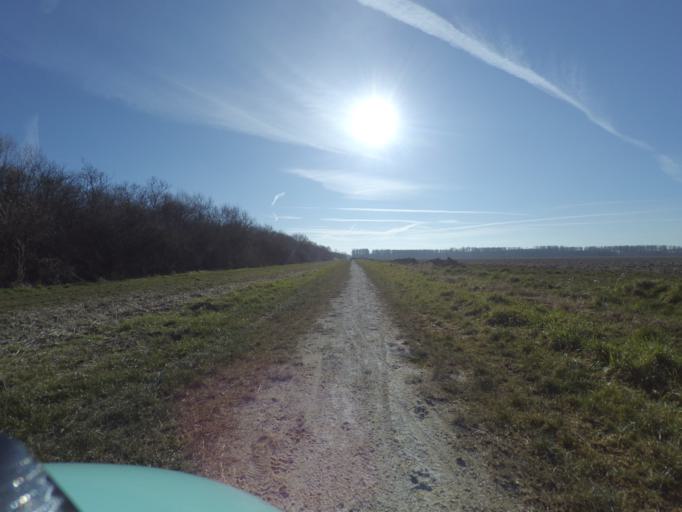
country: NL
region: Flevoland
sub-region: Gemeente Almere
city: Almere Stad
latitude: 52.3922
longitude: 5.1634
